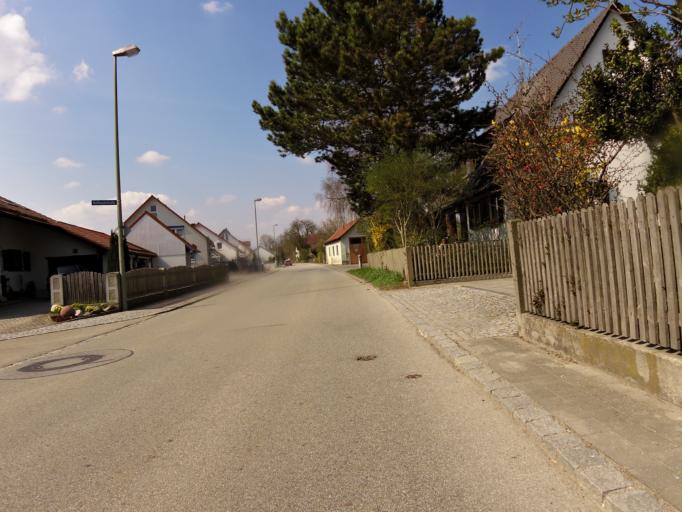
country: DE
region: Bavaria
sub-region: Upper Bavaria
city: Wang
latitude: 48.4949
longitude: 11.9622
